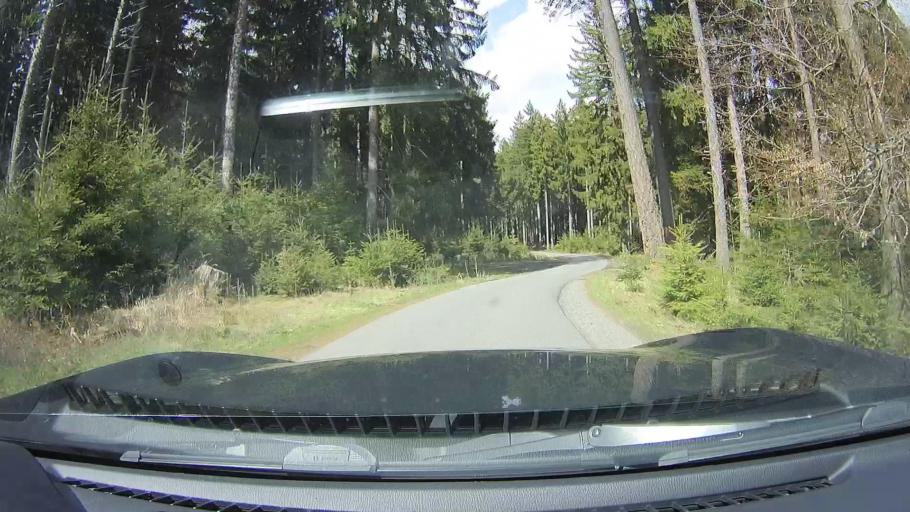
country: DE
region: Hesse
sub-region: Regierungsbezirk Darmstadt
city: Hesseneck
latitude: 49.5926
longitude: 9.0862
